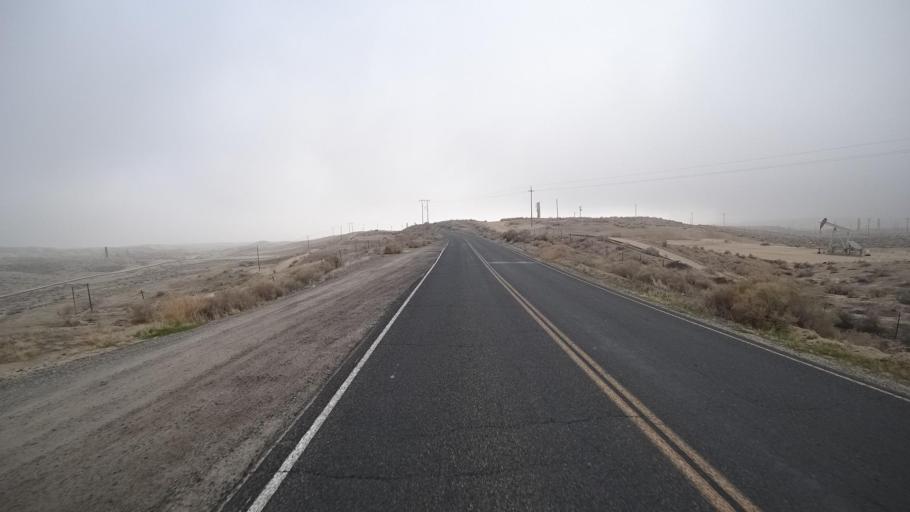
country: US
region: California
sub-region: Kern County
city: Ford City
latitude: 35.2627
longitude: -119.4629
